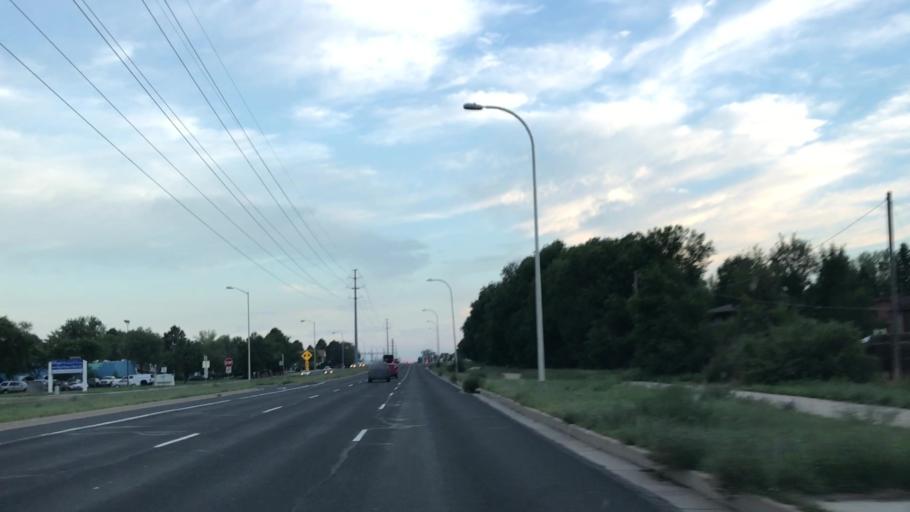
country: US
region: Colorado
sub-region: El Paso County
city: Cimarron Hills
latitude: 38.8653
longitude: -104.7573
